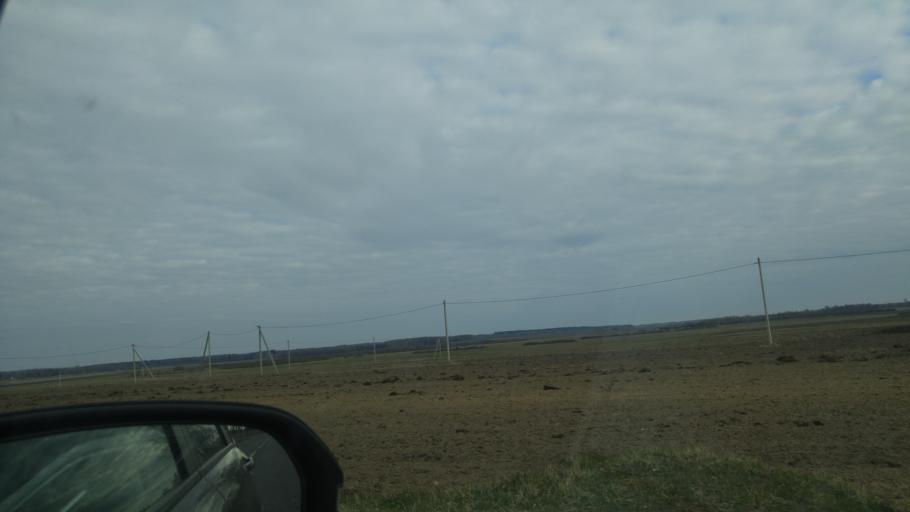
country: BY
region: Minsk
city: Chervyen'
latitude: 53.6157
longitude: 28.6943
